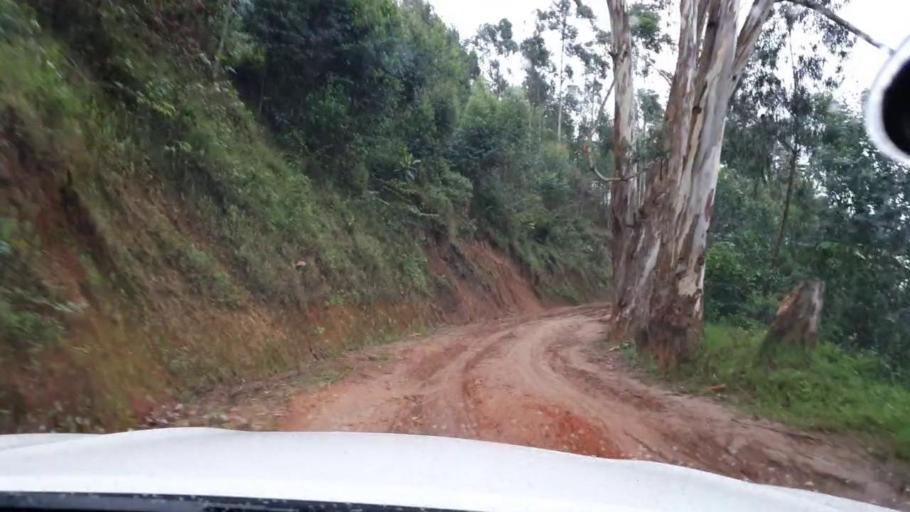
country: RW
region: Western Province
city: Cyangugu
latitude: -2.4118
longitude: 29.1873
